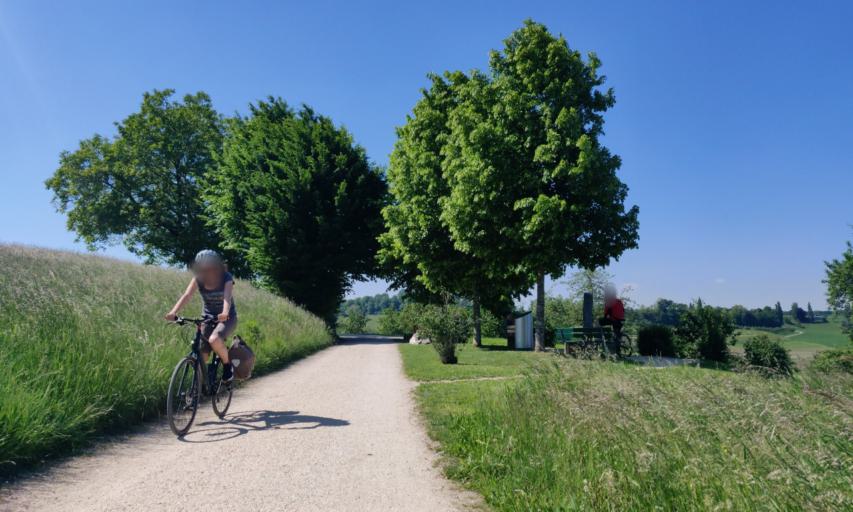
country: CH
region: Basel-Landschaft
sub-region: Bezirk Arlesheim
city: Pfeffingen
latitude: 47.4703
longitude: 7.5820
